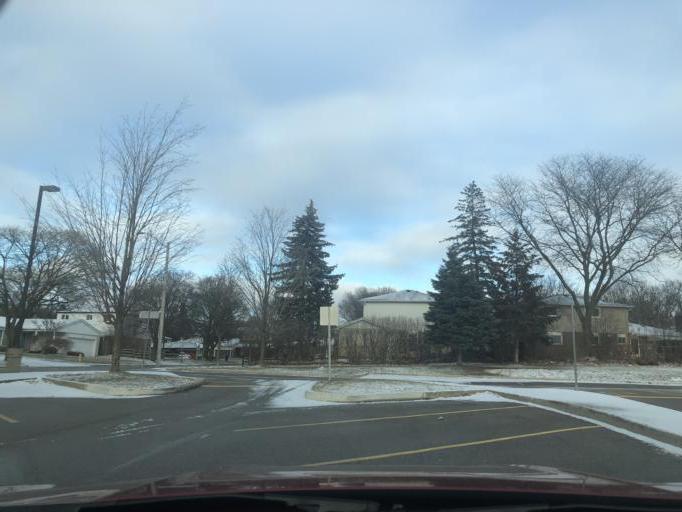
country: CA
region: Ontario
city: Markham
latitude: 43.8752
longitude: -79.2432
